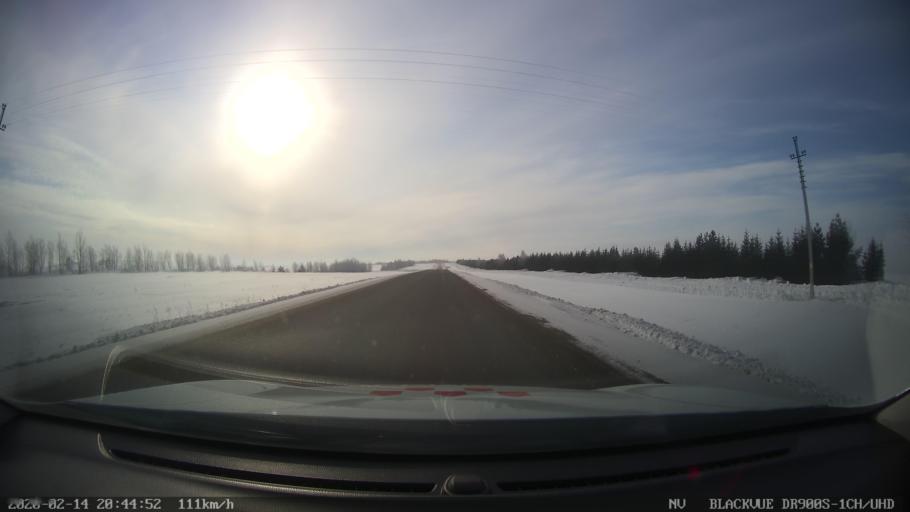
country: RU
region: Tatarstan
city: Kuybyshevskiy Zaton
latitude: 55.2868
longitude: 49.1449
